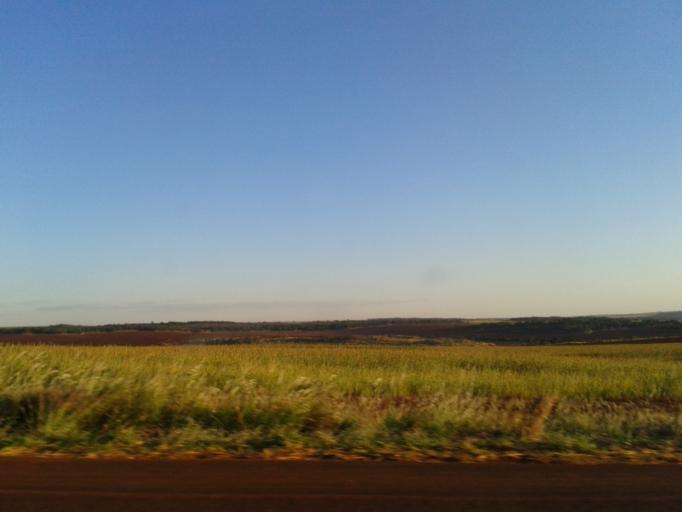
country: BR
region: Minas Gerais
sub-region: Centralina
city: Centralina
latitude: -18.7311
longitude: -49.2599
